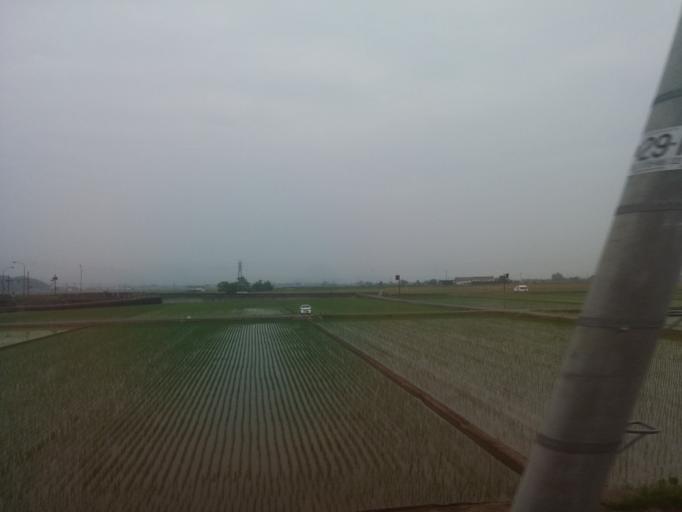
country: JP
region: Shiga Prefecture
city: Youkaichi
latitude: 35.1643
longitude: 136.1540
